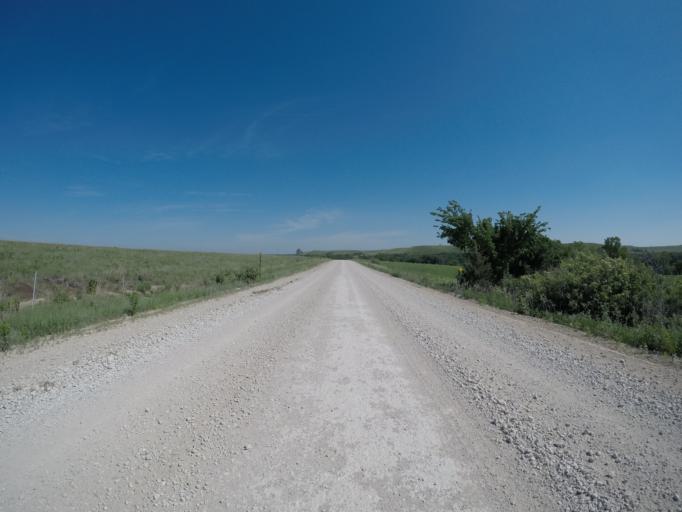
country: US
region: Kansas
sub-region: Wabaunsee County
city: Alma
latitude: 39.0166
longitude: -96.1413
